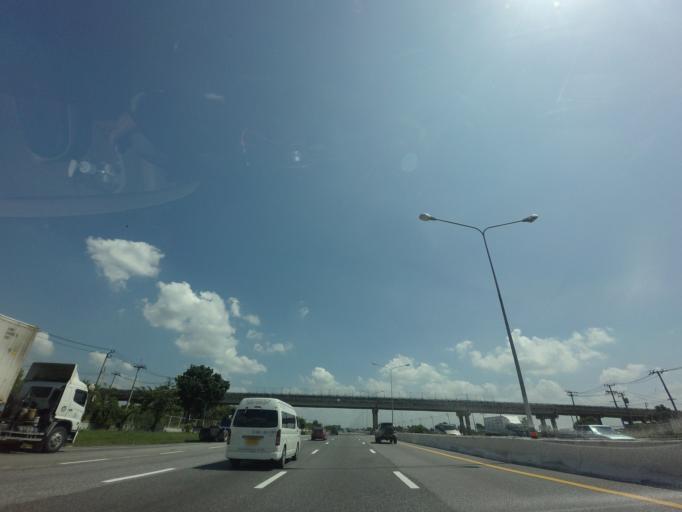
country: TH
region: Samut Prakan
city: Ban Khlong Bang Sao Thong
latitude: 13.6164
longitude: 100.9274
